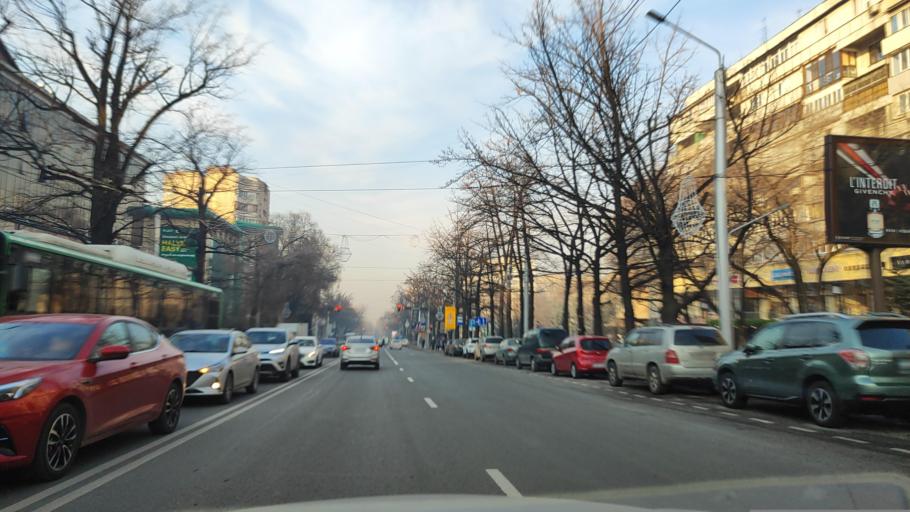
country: KZ
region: Almaty Qalasy
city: Almaty
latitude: 43.2510
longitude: 76.9560
